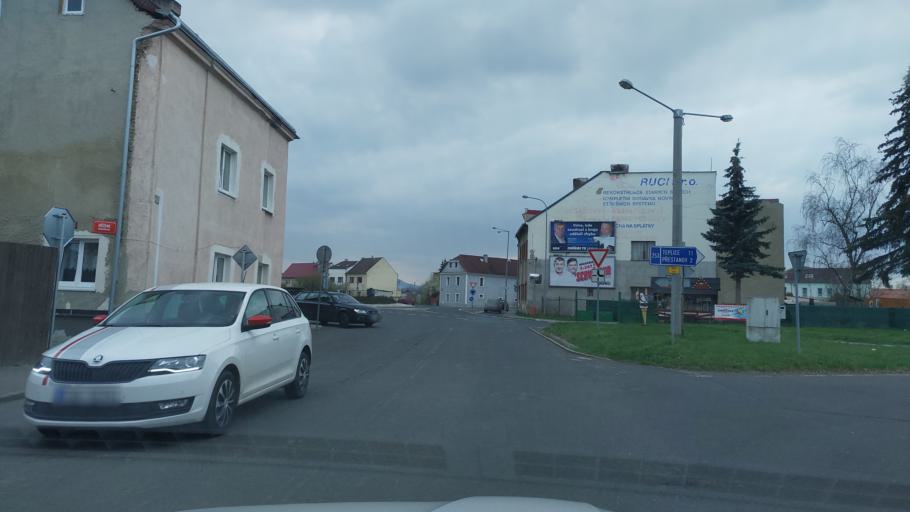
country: CZ
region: Ustecky
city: Chabarovice
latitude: 50.6750
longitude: 13.9378
